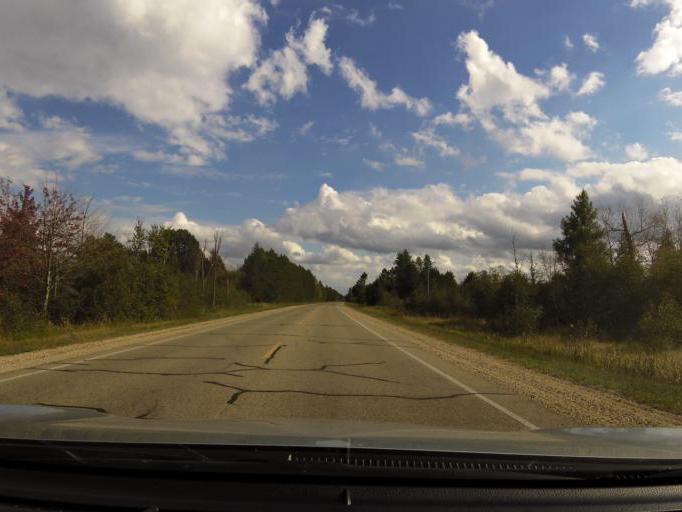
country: US
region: Michigan
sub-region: Roscommon County
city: Saint Helen
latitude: 44.3952
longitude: -84.4367
